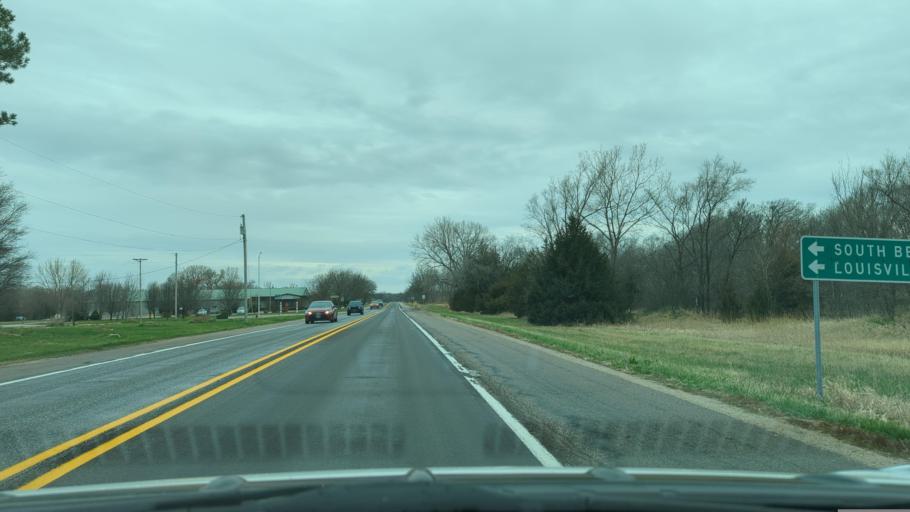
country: US
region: Nebraska
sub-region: Lancaster County
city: Waverly
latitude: 40.9590
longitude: -96.4450
